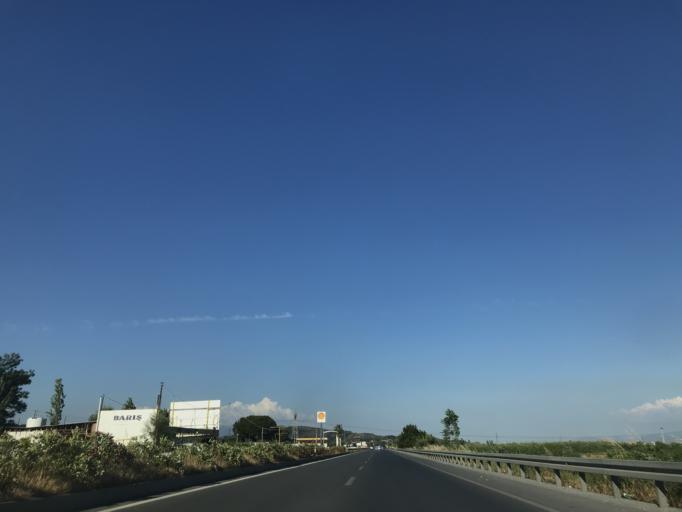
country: TR
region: Aydin
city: Ortaklar
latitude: 37.8314
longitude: 27.5066
